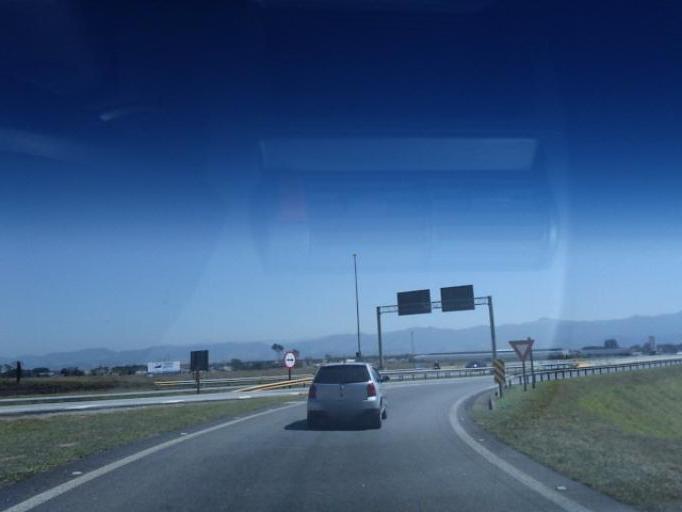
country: BR
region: Sao Paulo
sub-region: Taubate
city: Taubate
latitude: -23.0607
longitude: -45.6199
